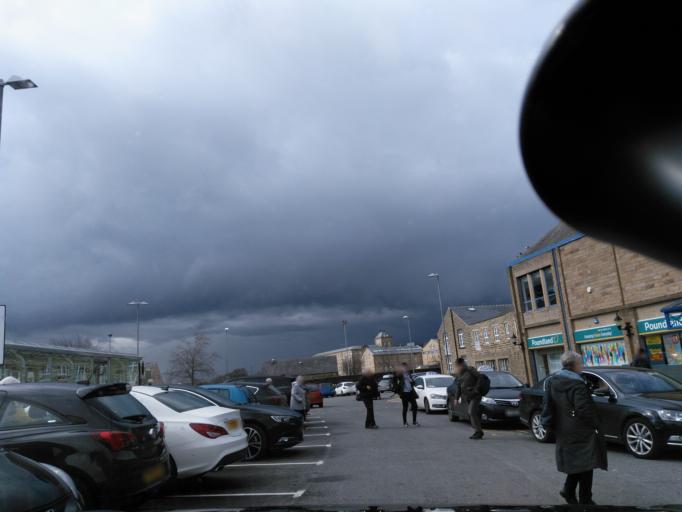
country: GB
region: England
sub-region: North Yorkshire
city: Skipton
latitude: 53.9595
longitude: -2.0184
